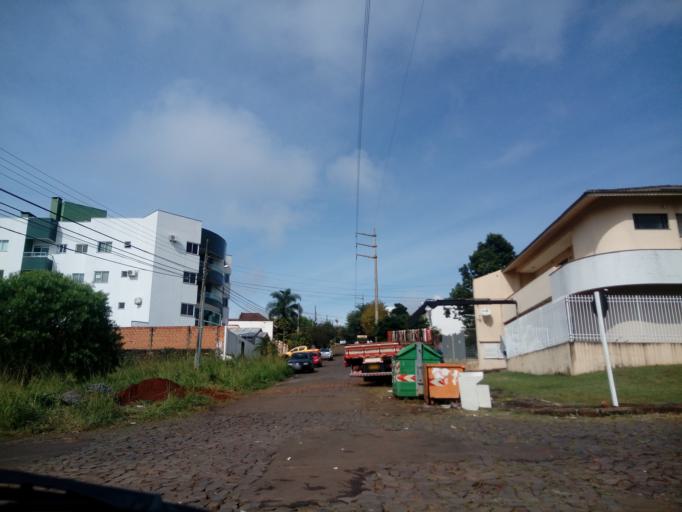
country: BR
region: Santa Catarina
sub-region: Chapeco
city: Chapeco
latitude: -27.1000
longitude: -52.6015
